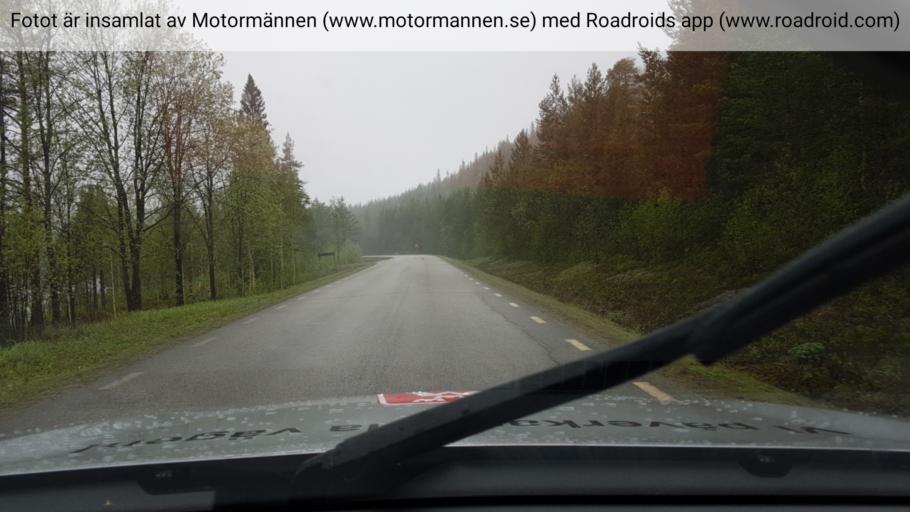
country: SE
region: Jaemtland
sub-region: Bergs Kommun
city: Hoverberg
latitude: 63.0355
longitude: 14.0414
